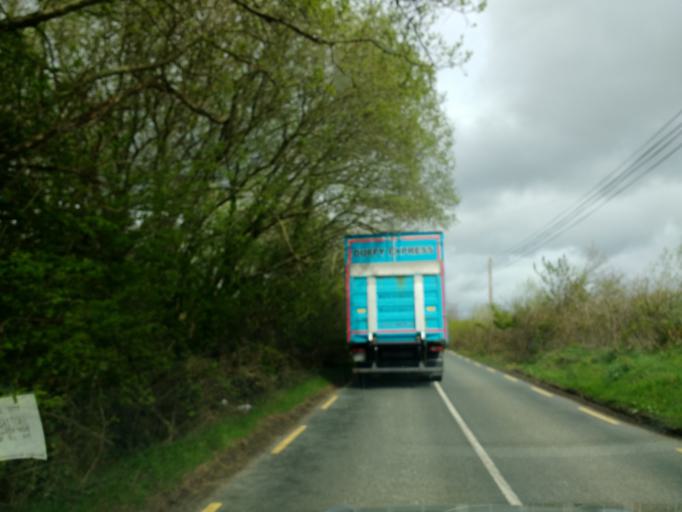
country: IE
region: Ulster
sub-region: County Donegal
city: Ramelton
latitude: 55.0777
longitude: -7.5913
